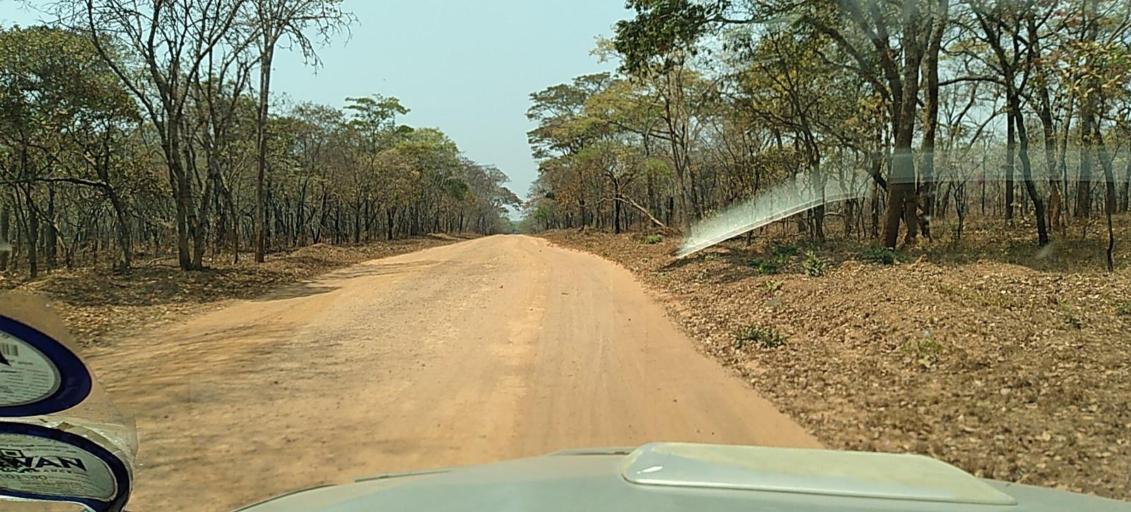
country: ZM
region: North-Western
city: Kasempa
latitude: -13.5578
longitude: 26.0762
